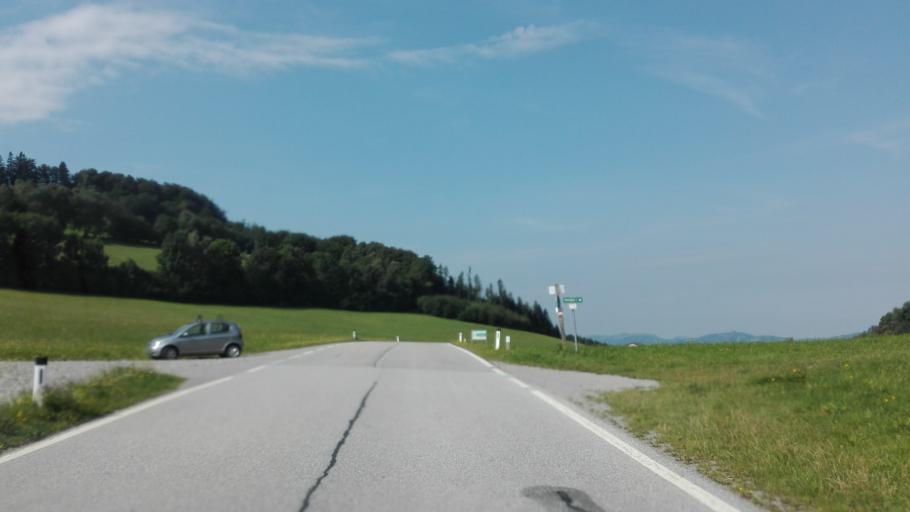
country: AT
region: Lower Austria
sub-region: Politischer Bezirk Lilienfeld
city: Eschenau
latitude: 48.0362
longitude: 15.5203
